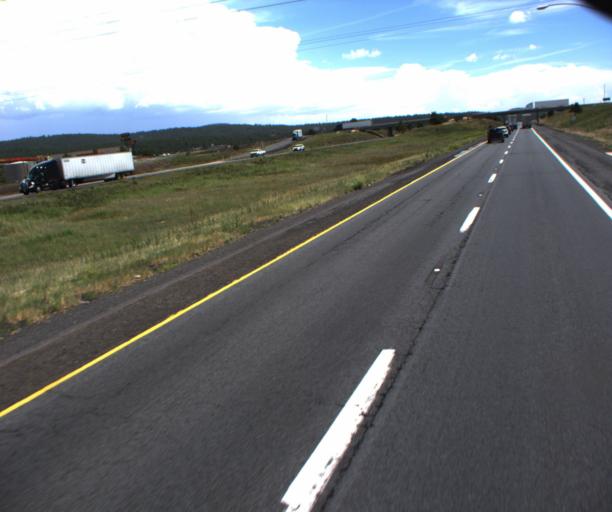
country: US
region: Arizona
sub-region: Coconino County
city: Parks
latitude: 35.2377
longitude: -111.8263
